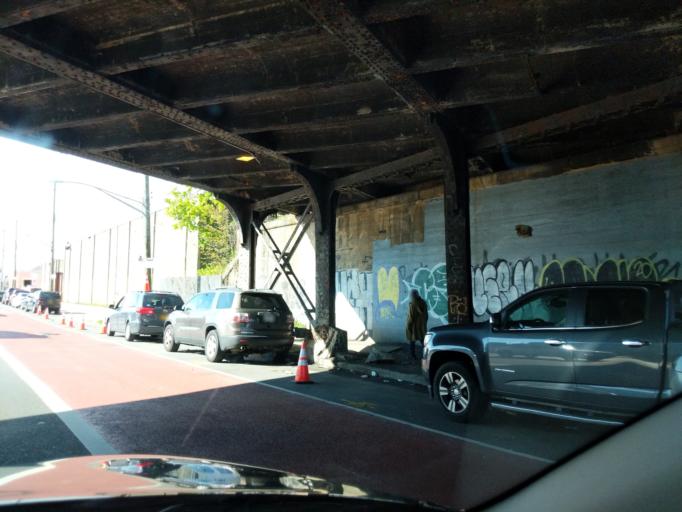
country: US
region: New York
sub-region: Kings County
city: Brooklyn
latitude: 40.6368
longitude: -73.9288
